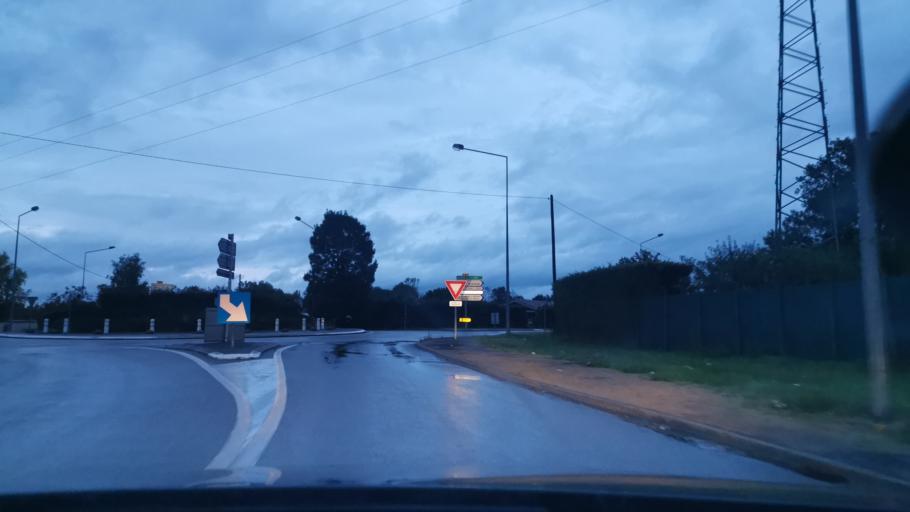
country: FR
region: Rhone-Alpes
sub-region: Departement de l'Ain
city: Crottet
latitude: 46.2888
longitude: 4.9120
